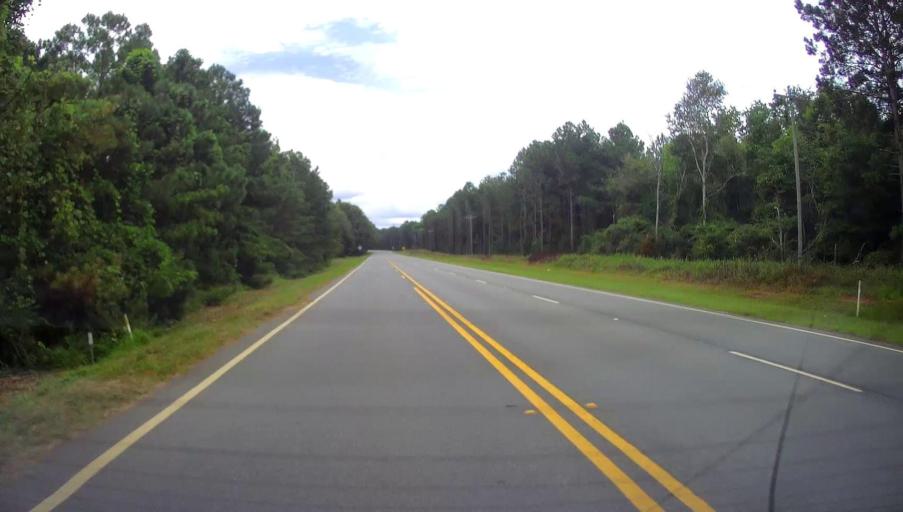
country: US
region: Georgia
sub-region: Schley County
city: Ellaville
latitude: 32.2589
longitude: -84.2449
